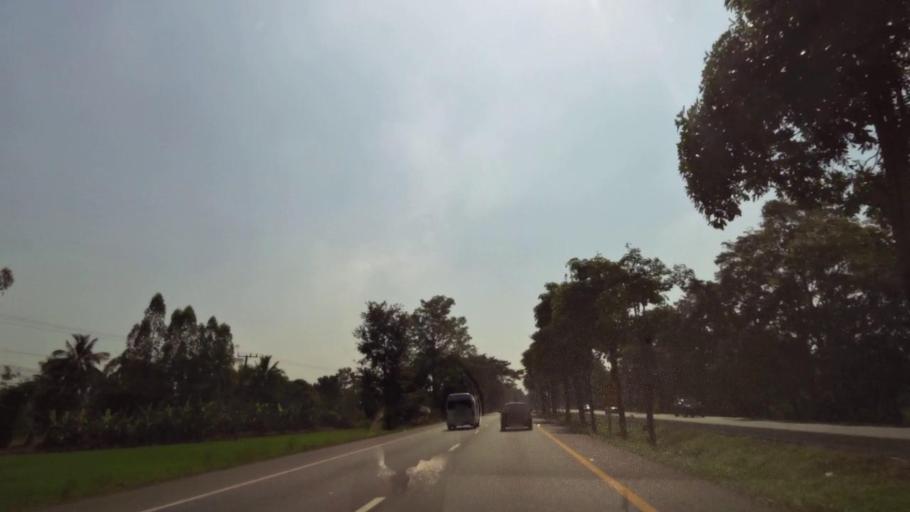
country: TH
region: Phichit
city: Bueng Na Rang
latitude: 16.0655
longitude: 100.1235
